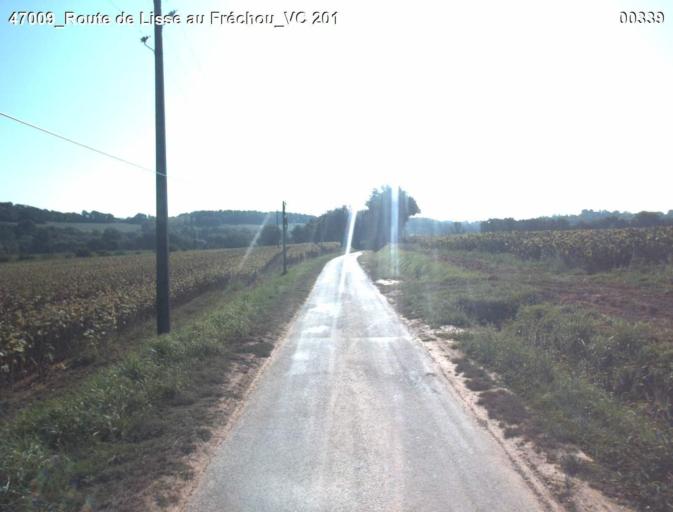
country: FR
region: Aquitaine
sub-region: Departement du Lot-et-Garonne
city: Nerac
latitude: 44.0938
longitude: 0.3066
